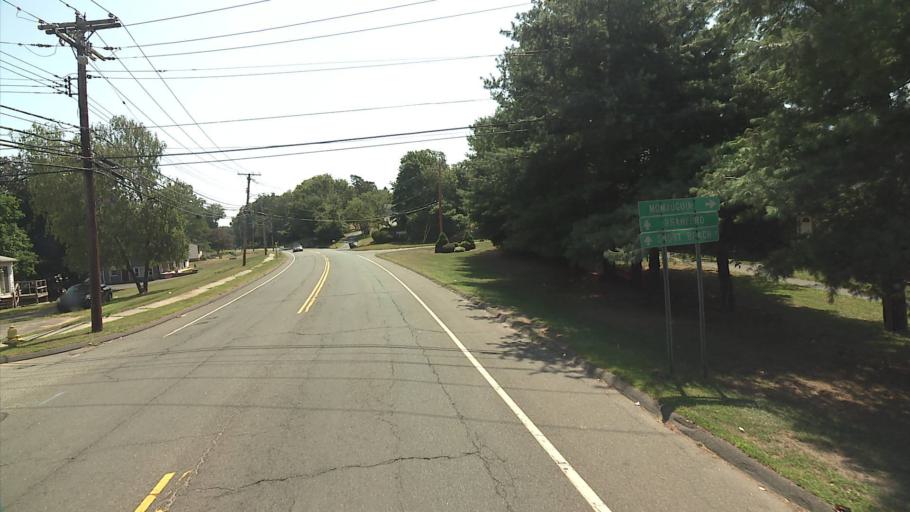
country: US
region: Connecticut
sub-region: New Haven County
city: East Haven
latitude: 41.2622
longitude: -72.8663
